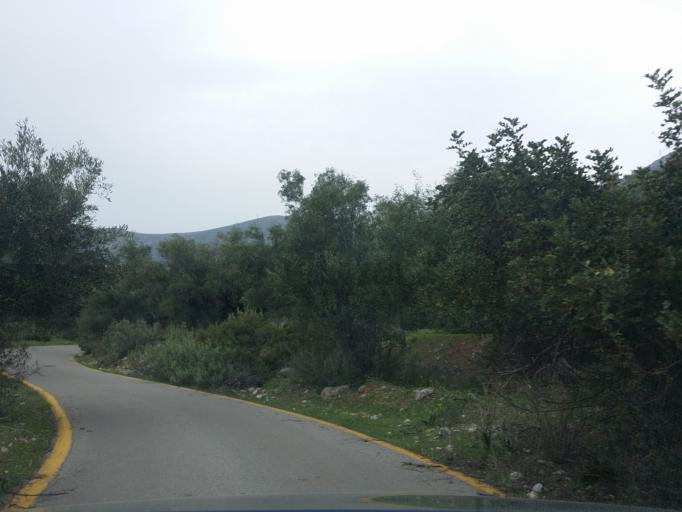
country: GR
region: Central Greece
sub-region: Nomos Voiotias
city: Kaparellion
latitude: 38.1482
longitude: 23.2311
